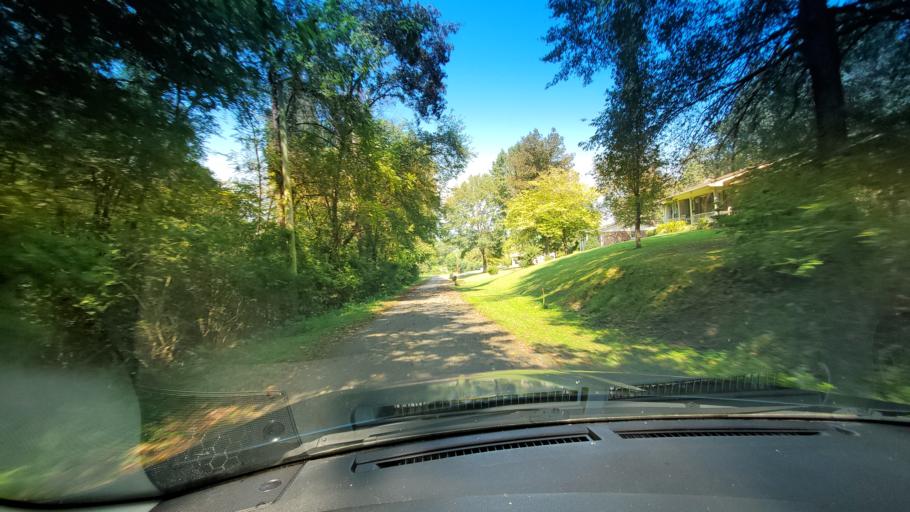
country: US
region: Tennessee
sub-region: Smith County
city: Carthage
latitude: 36.2500
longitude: -85.9607
